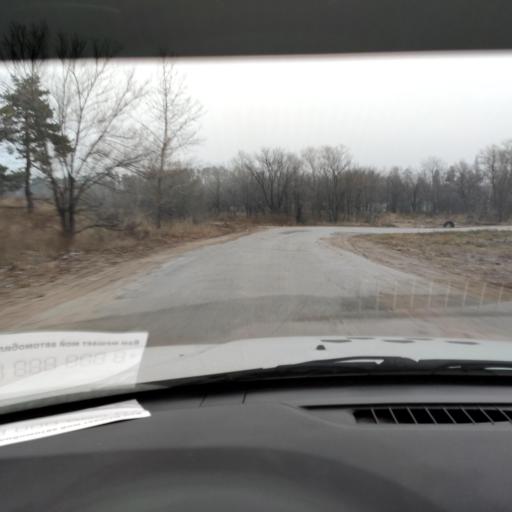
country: RU
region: Samara
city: Zhigulevsk
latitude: 53.4700
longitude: 49.5619
